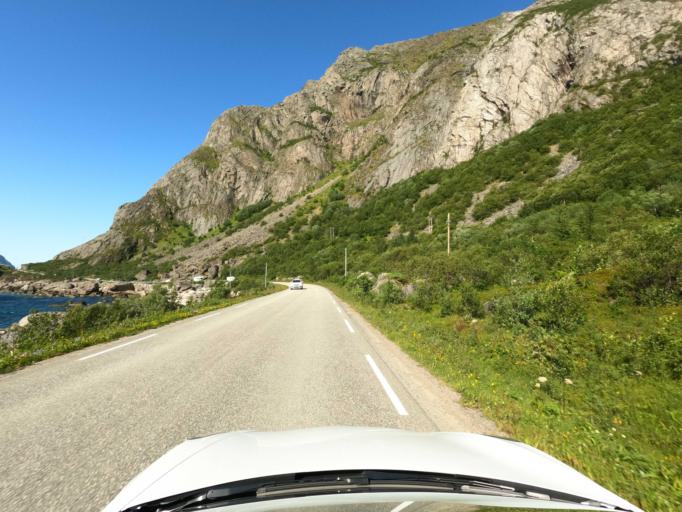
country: NO
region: Nordland
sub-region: Vagan
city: Kabelvag
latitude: 68.2100
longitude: 14.2219
